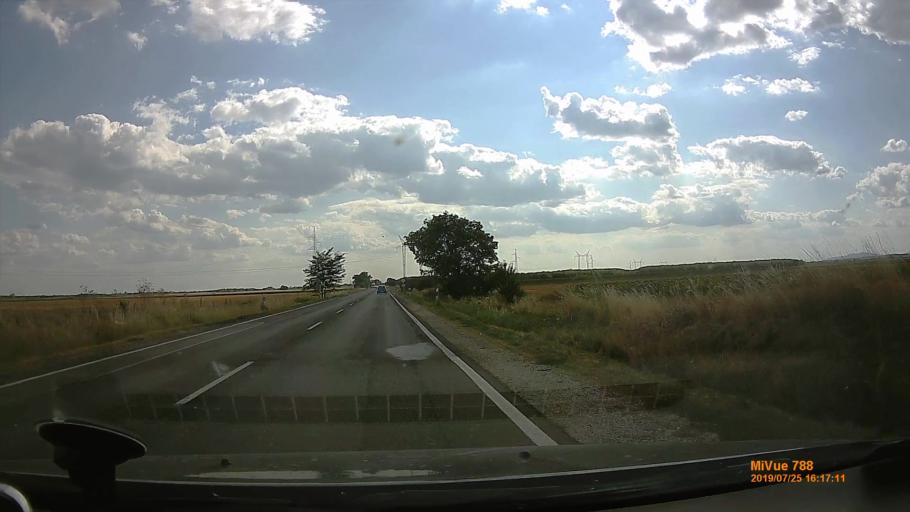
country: HU
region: Heves
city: Kal
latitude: 47.7717
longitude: 20.2795
